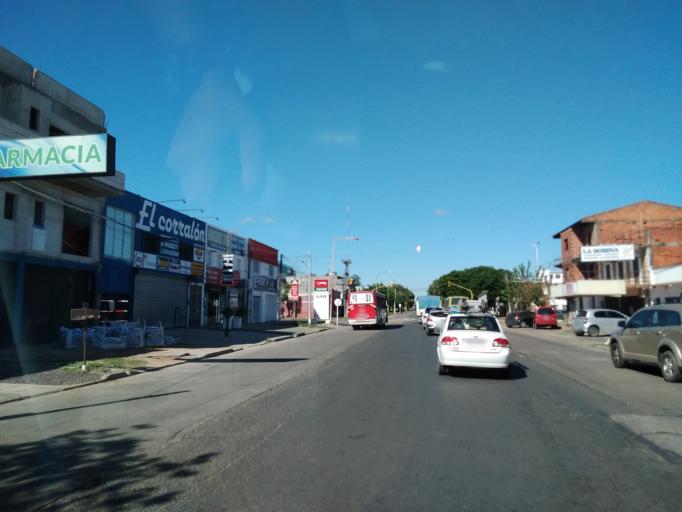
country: AR
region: Corrientes
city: Corrientes
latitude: -27.4711
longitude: -58.8135
